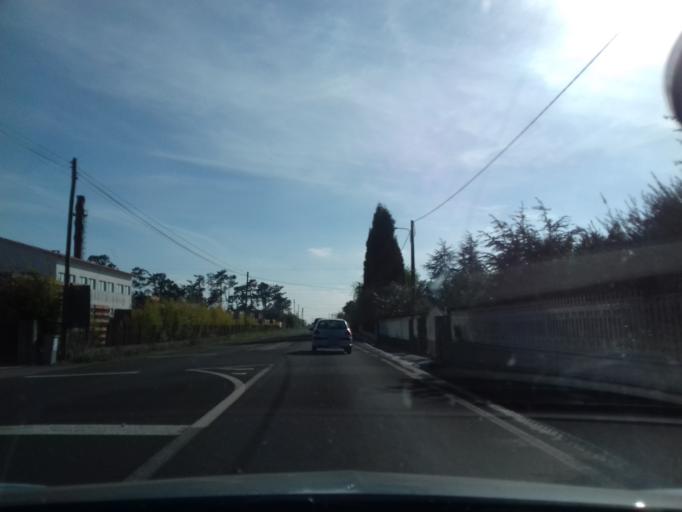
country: PT
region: Leiria
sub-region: Leiria
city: Maceira
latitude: 39.7015
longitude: -8.8723
